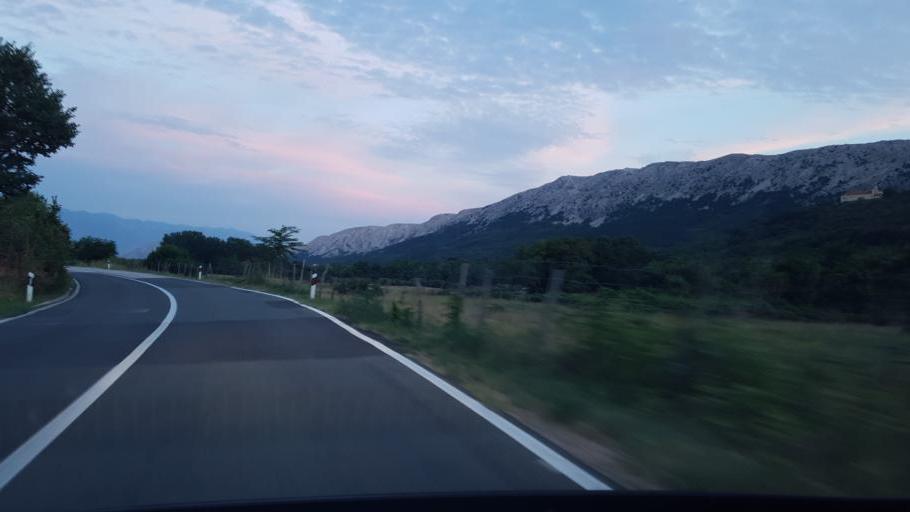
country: HR
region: Primorsko-Goranska
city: Punat
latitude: 44.9843
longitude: 14.7249
